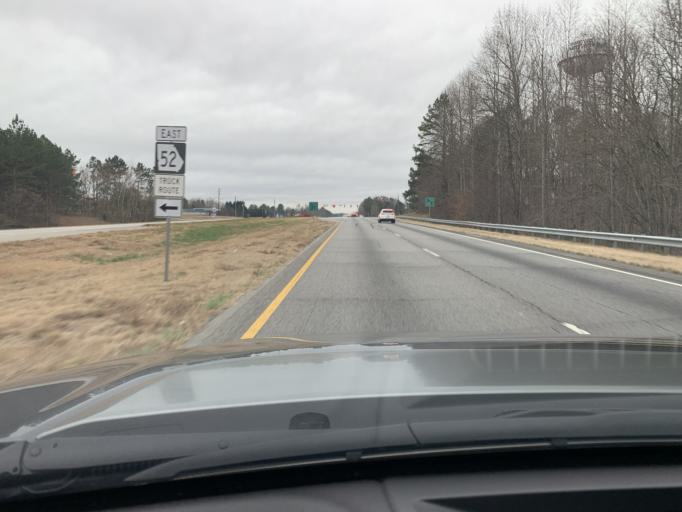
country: US
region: Georgia
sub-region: Hall County
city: Lula
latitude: 34.3967
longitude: -83.6888
